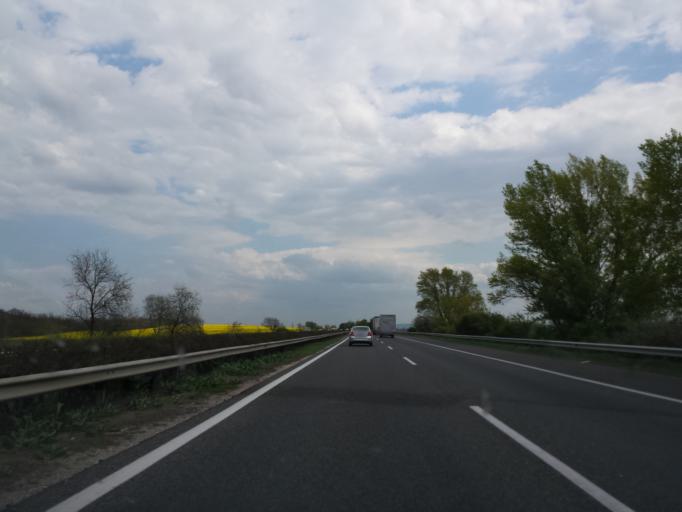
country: HU
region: Komarom-Esztergom
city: Mocsa
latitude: 47.6483
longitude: 18.2049
